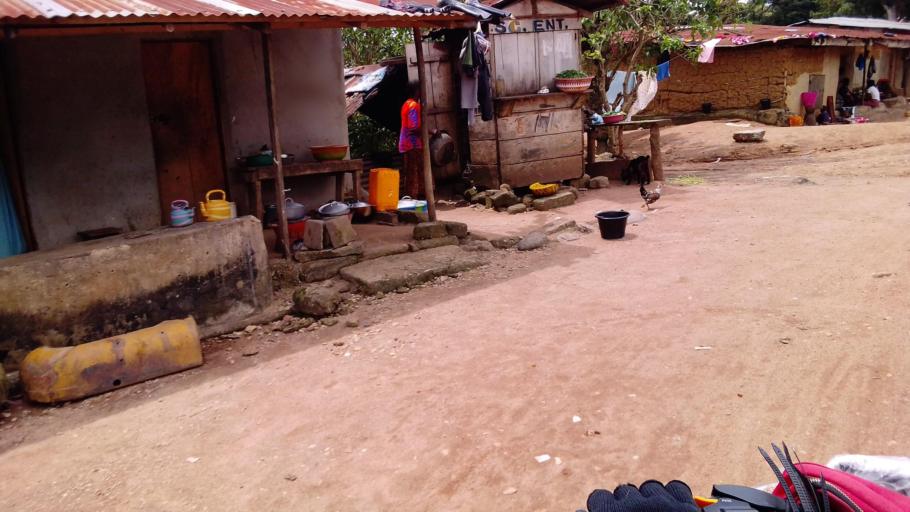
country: SL
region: Eastern Province
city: Koidu
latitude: 8.6747
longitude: -10.9966
